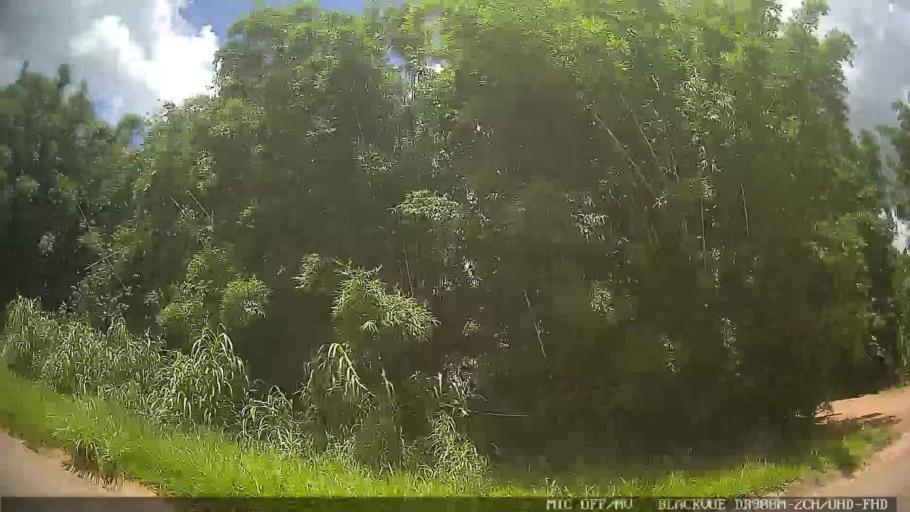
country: BR
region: Sao Paulo
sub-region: Braganca Paulista
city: Braganca Paulista
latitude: -22.8381
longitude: -46.6631
